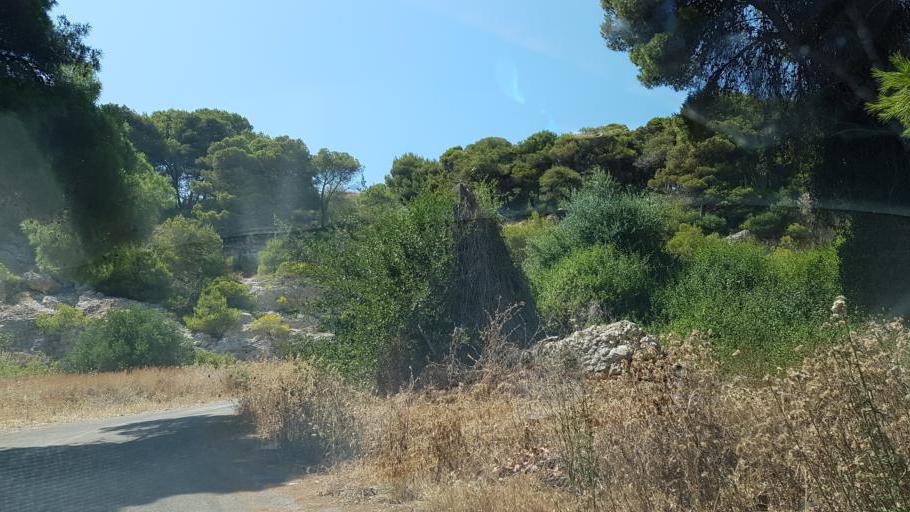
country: IT
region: Apulia
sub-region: Provincia di Lecce
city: Nardo
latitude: 40.1427
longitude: 17.9802
